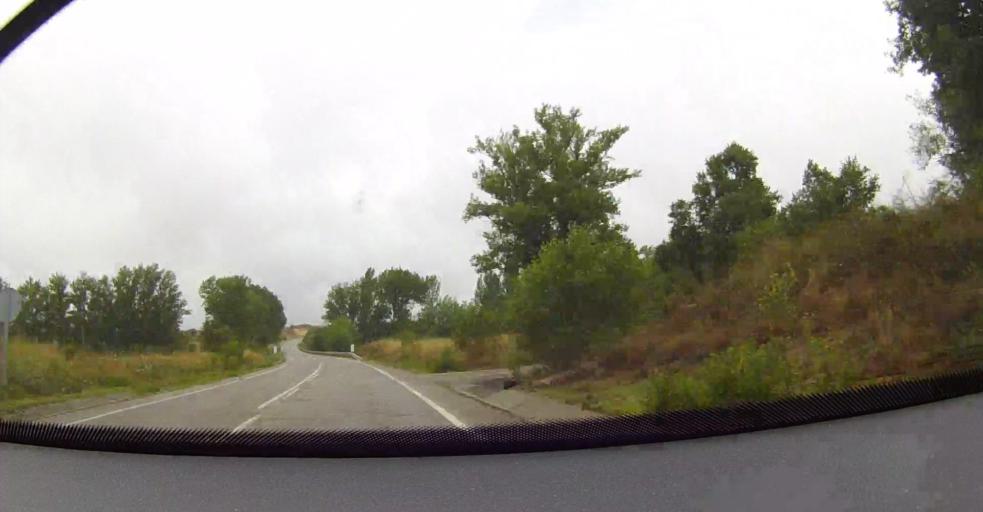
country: ES
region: Castille and Leon
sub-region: Provincia de Leon
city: Bonar
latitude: 42.8456
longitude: -5.2647
